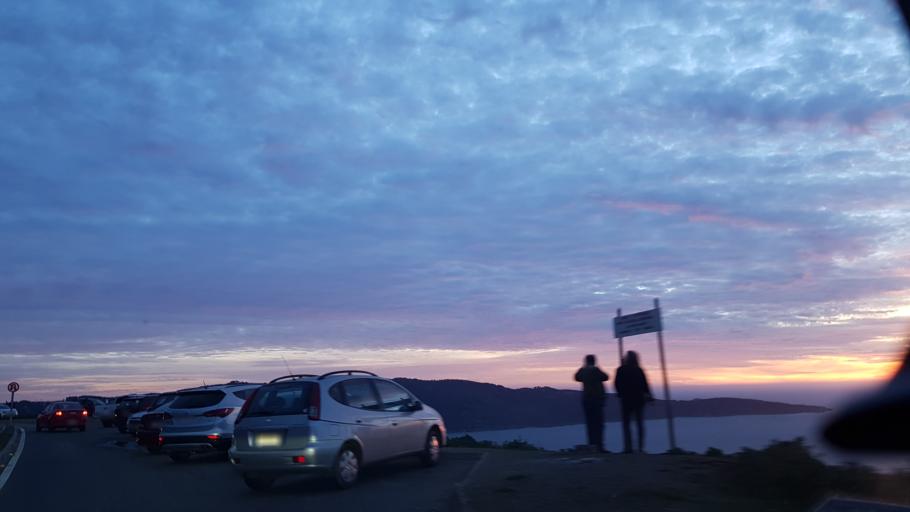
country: CL
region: Valparaiso
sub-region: Provincia de Valparaiso
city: Valparaiso
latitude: -33.0819
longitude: -71.6627
